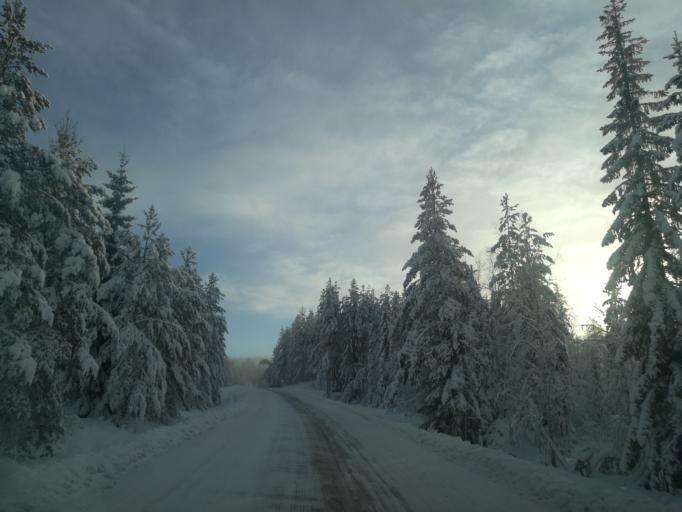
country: SE
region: Vaermland
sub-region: Torsby Kommun
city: Torsby
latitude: 60.6500
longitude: 12.8938
